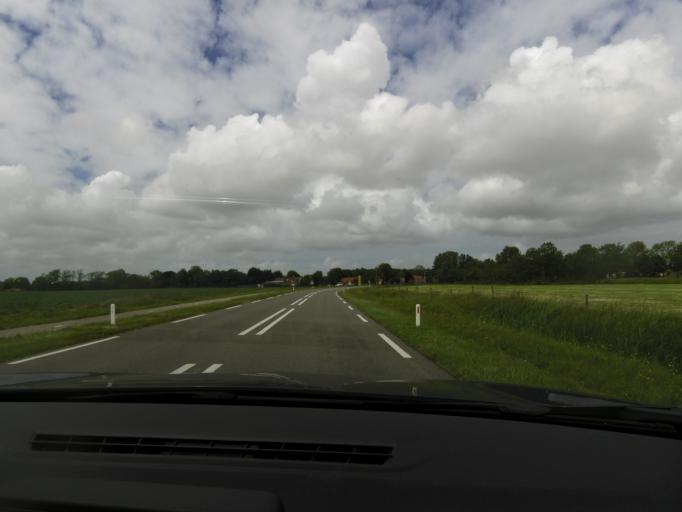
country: NL
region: Zeeland
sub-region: Schouwen-Duiveland
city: Scharendijke
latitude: 51.6910
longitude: 3.9362
